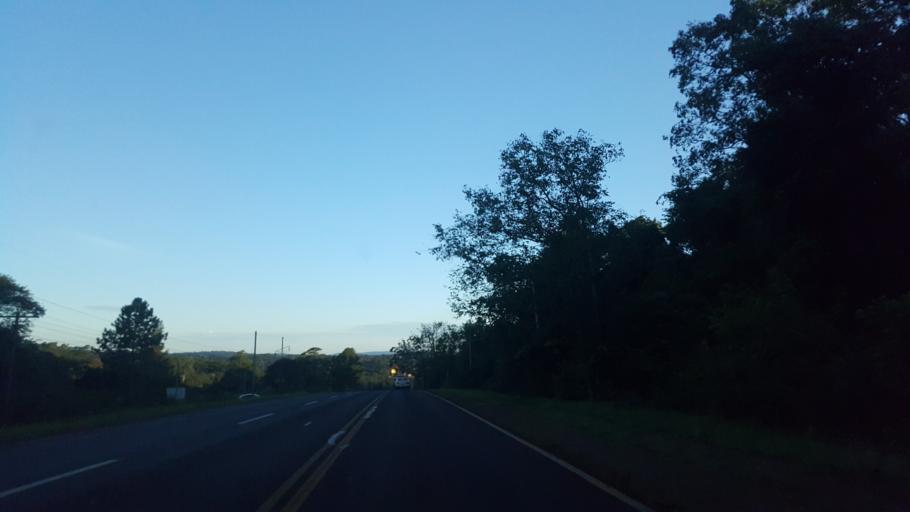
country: AR
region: Misiones
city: Capiovi
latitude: -26.9151
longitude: -55.0597
